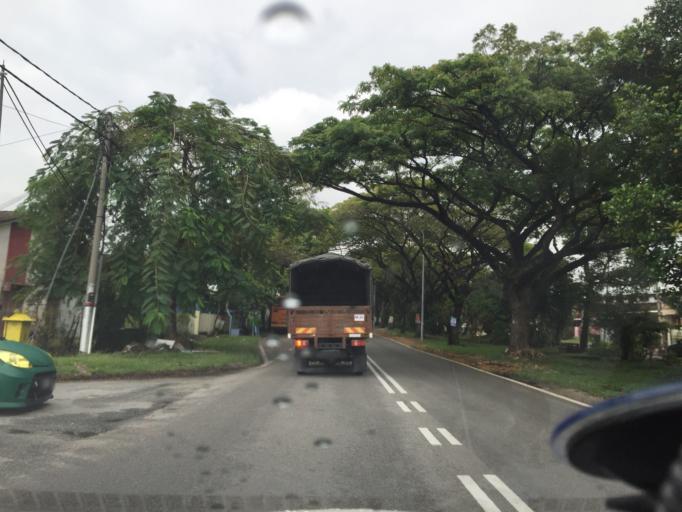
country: MY
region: Selangor
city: Klang
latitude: 3.0098
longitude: 101.4437
